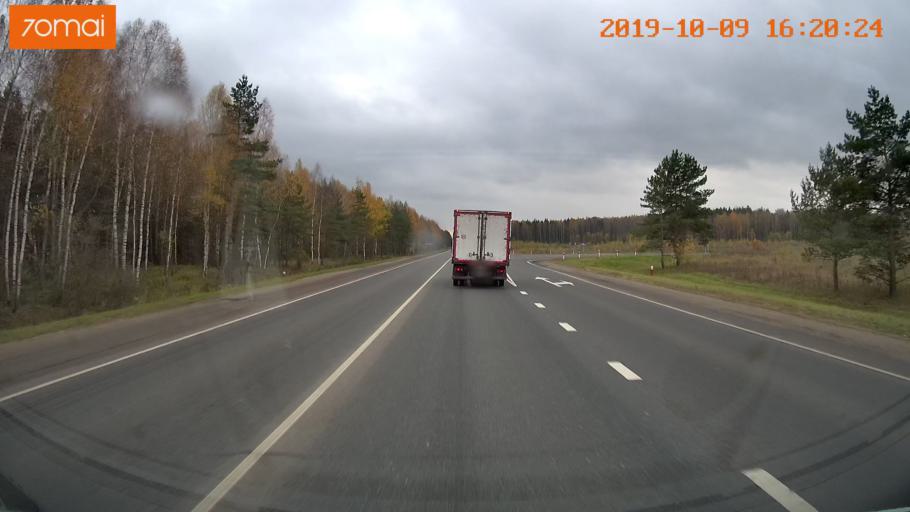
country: RU
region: Kostroma
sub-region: Kostromskoy Rayon
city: Kostroma
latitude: 57.7068
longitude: 40.8922
